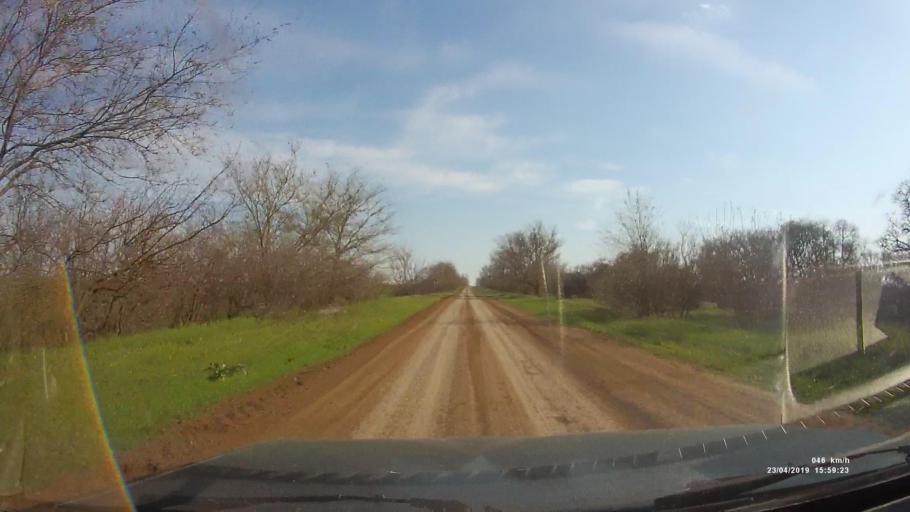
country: RU
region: Rostov
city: Remontnoye
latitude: 46.5172
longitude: 43.1096
